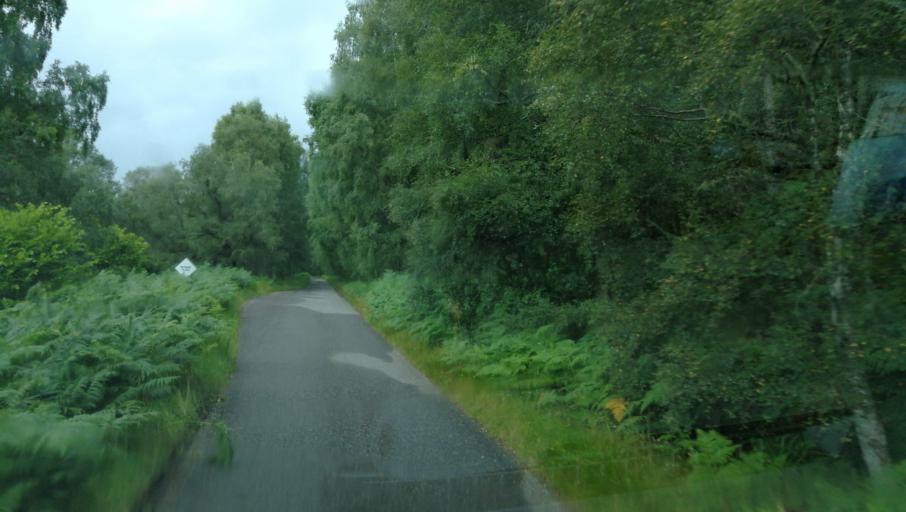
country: GB
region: Scotland
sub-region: Highland
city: Spean Bridge
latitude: 57.3016
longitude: -4.8826
